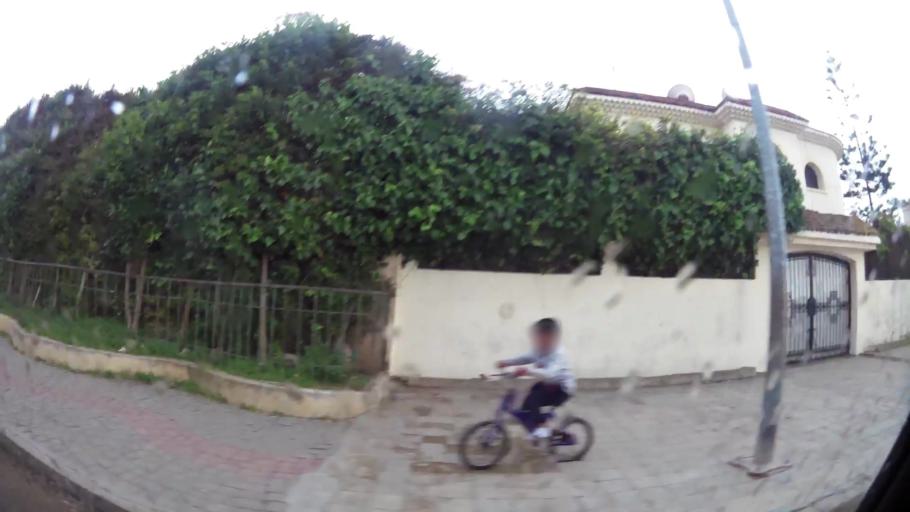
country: MA
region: Grand Casablanca
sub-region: Casablanca
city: Casablanca
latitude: 33.5774
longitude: -7.6836
